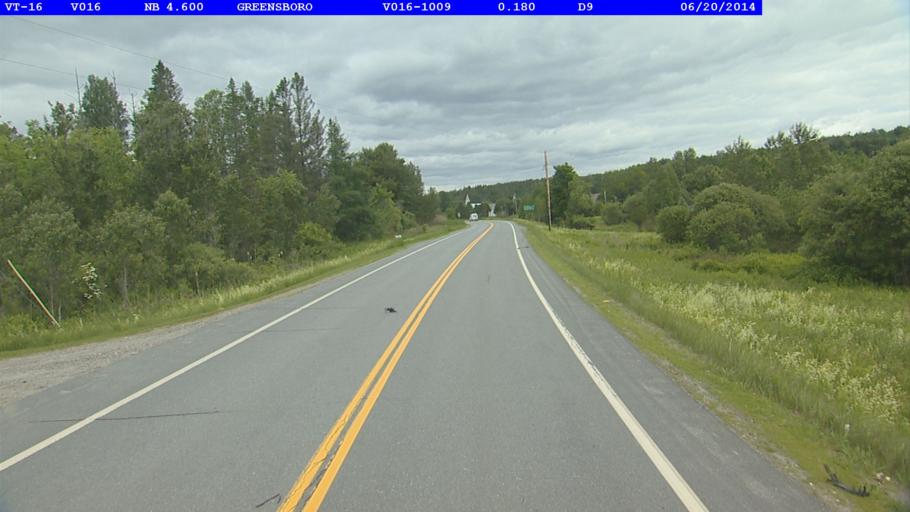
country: US
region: Vermont
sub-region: Caledonia County
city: Hardwick
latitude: 44.5469
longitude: -72.2668
